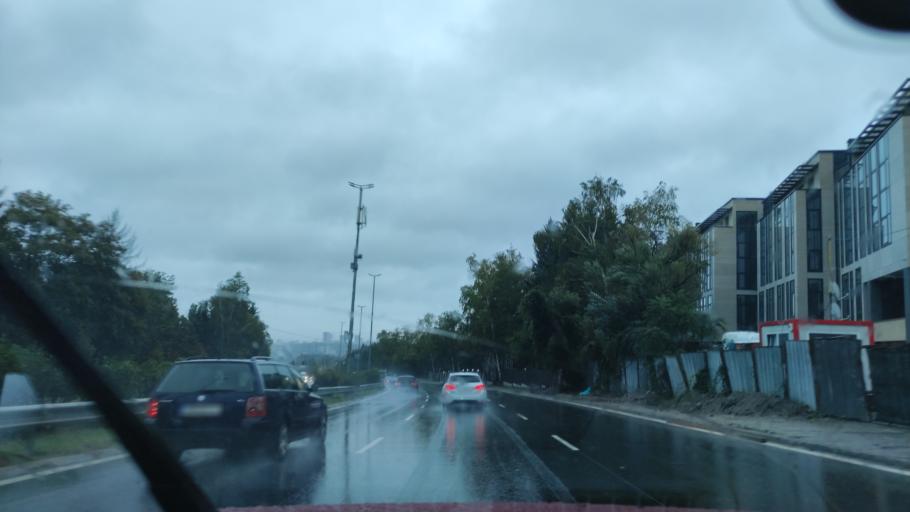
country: BG
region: Sofia-Capital
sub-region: Stolichna Obshtina
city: Sofia
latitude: 42.6492
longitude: 23.2759
